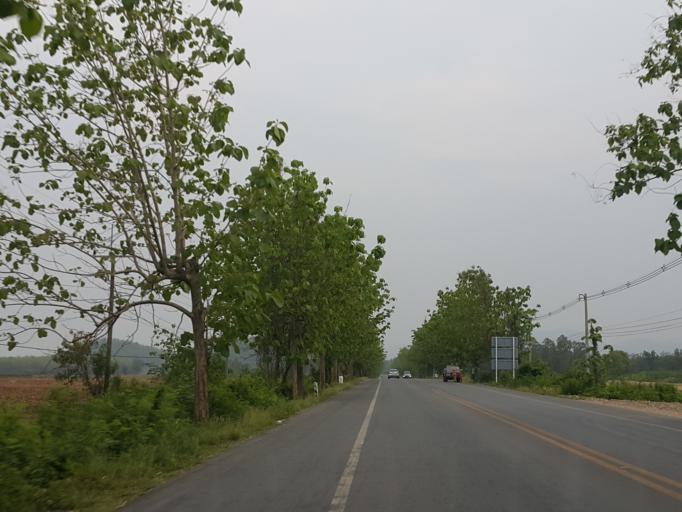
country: TH
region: Uthai Thani
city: Ban Rai
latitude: 15.0838
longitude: 99.5852
